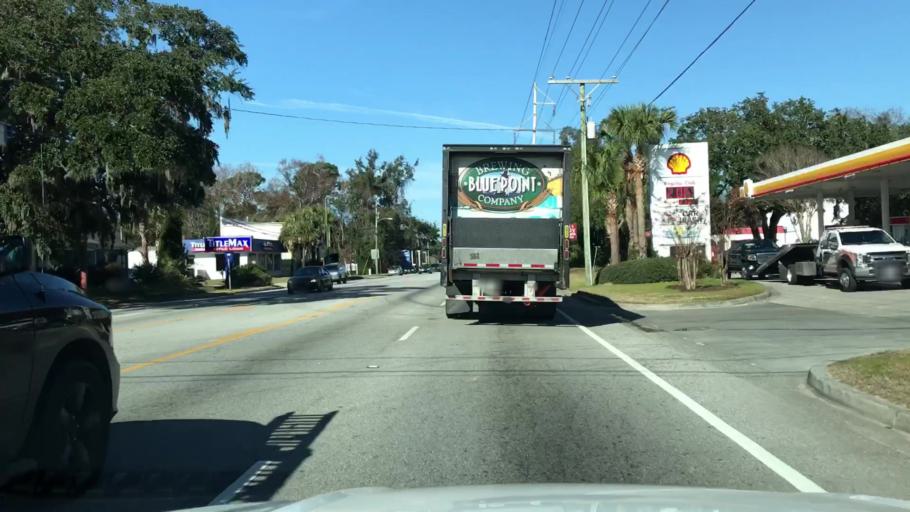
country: US
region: South Carolina
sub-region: Charleston County
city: Charleston
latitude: 32.7413
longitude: -79.9677
